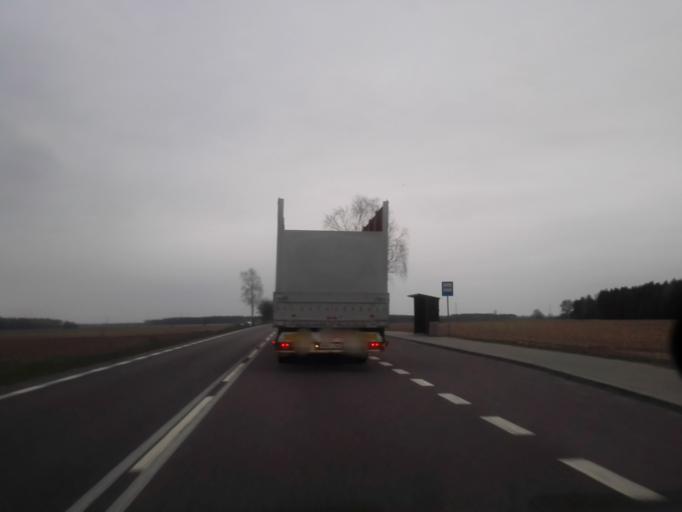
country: PL
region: Podlasie
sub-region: Powiat grajewski
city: Szczuczyn
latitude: 53.6021
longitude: 22.3618
